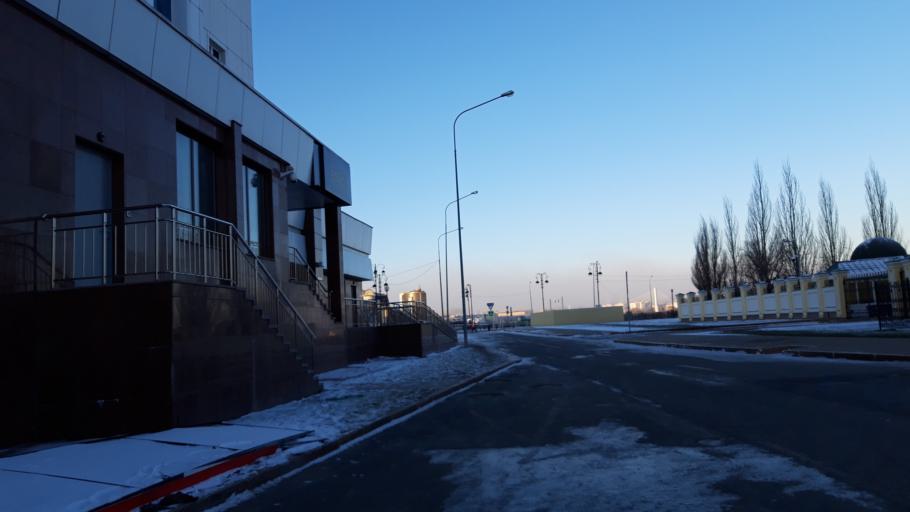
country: RU
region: Tjumen
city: Tyumen
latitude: 57.1607
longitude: 65.5438
